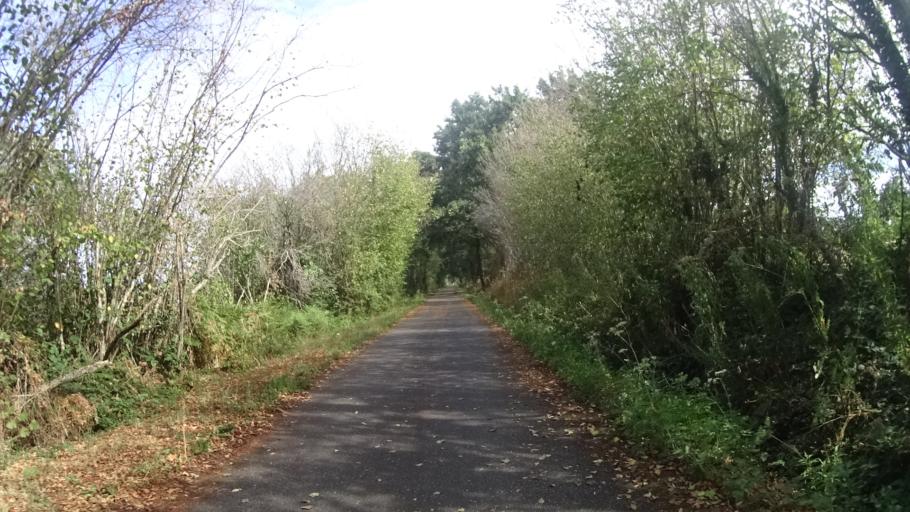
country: FR
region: Bourgogne
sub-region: Departement de Saone-et-Loire
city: Bourbon-Lancy
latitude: 46.5905
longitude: 3.7456
